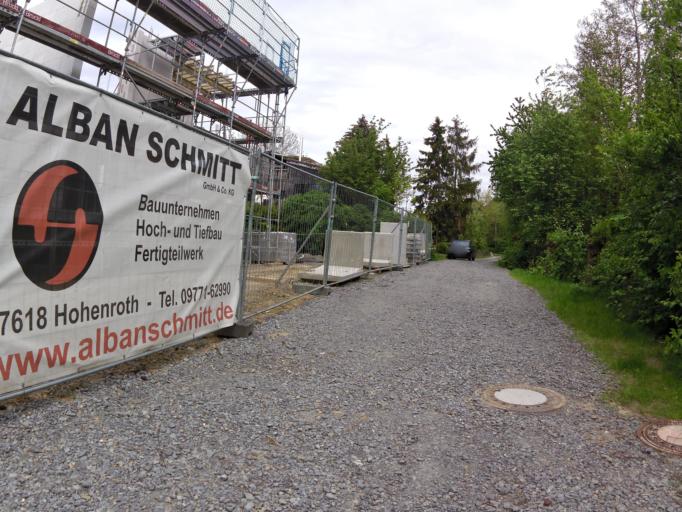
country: DE
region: Bavaria
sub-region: Regierungsbezirk Unterfranken
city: Kurnach
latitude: 49.8442
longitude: 10.0387
